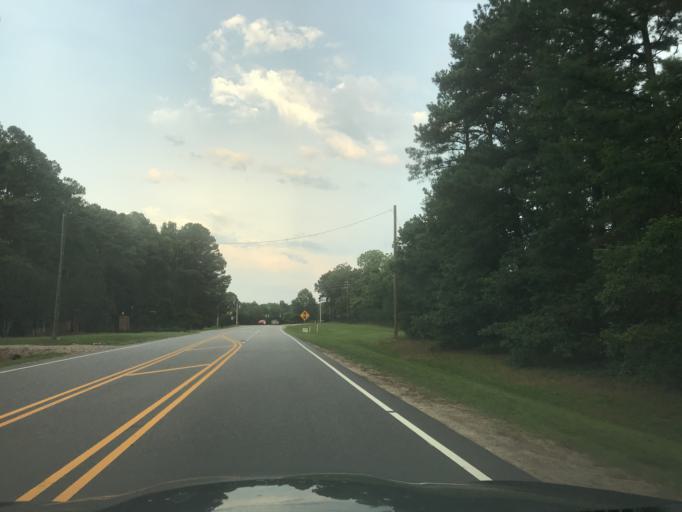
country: US
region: North Carolina
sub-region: Wake County
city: Wake Forest
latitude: 35.9176
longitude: -78.5969
